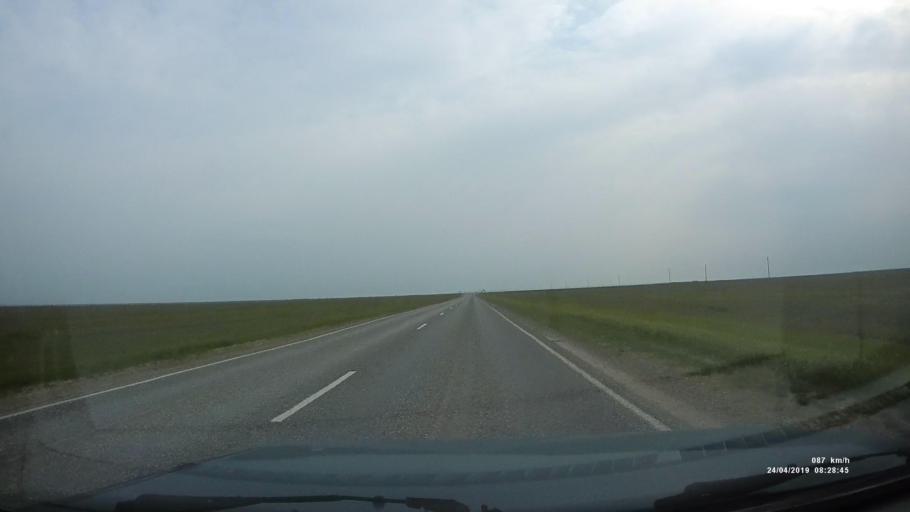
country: RU
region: Kalmykiya
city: Priyutnoye
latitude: 46.1469
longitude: 43.8205
